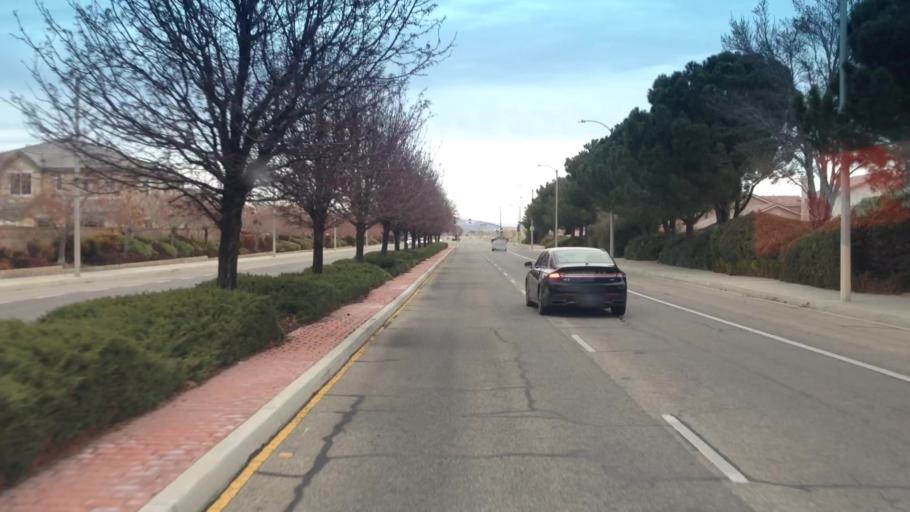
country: US
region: California
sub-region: Los Angeles County
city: Lancaster
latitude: 34.6946
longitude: -118.1839
